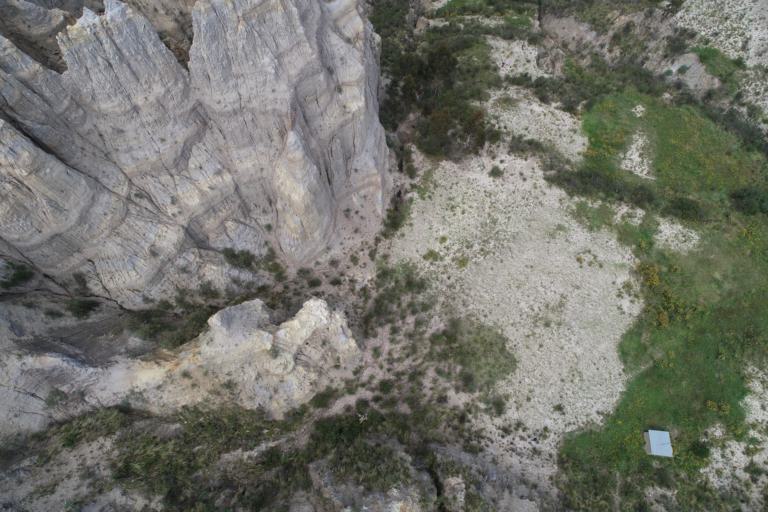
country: BO
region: La Paz
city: La Paz
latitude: -16.4996
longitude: -68.0636
